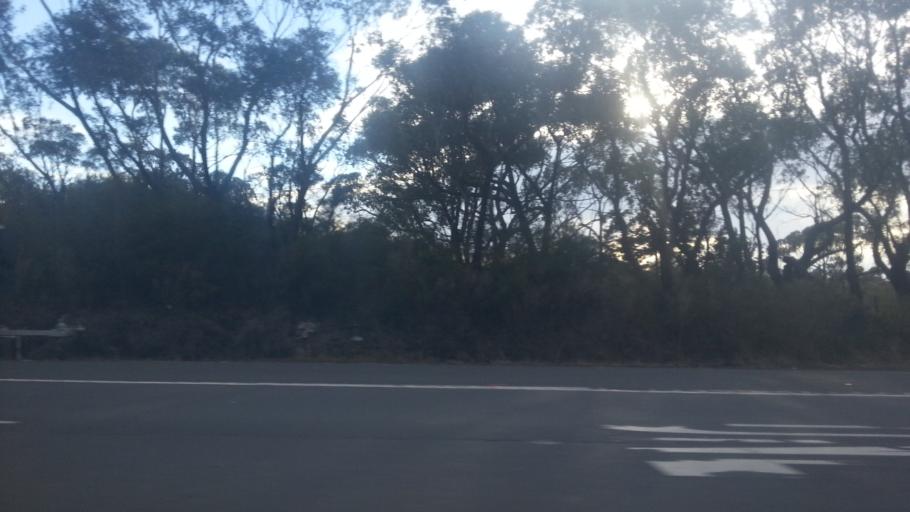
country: AU
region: New South Wales
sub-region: Wollongong
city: Bulli
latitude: -34.2980
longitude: 150.9055
